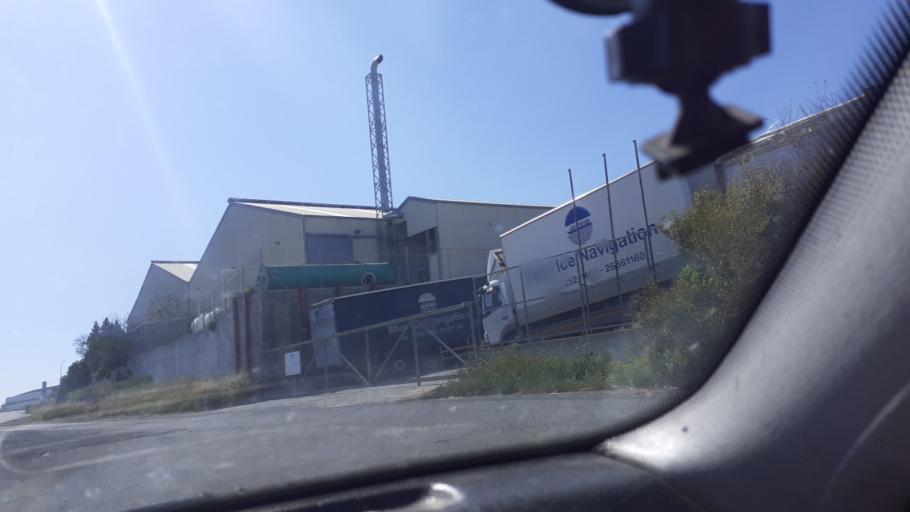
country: CY
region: Limassol
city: Ypsonas
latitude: 34.6646
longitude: 32.9932
